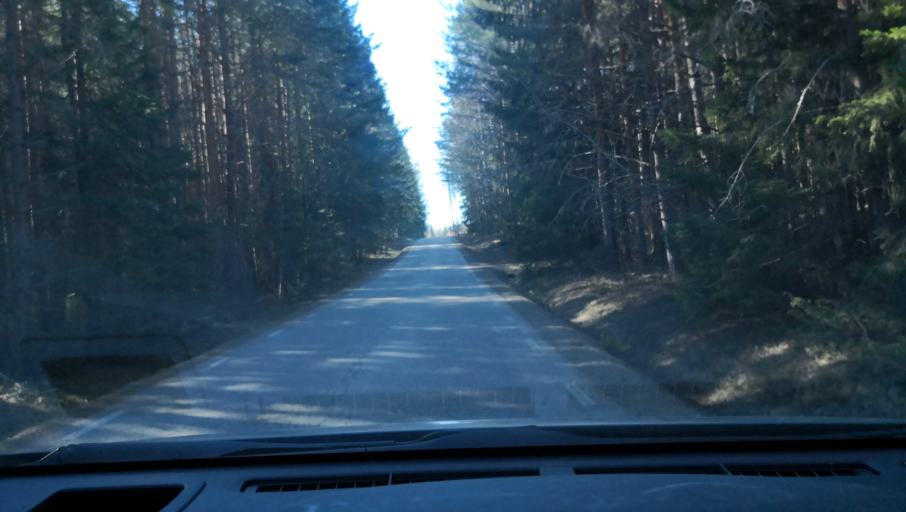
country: SE
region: Dalarna
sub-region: Avesta Kommun
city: Horndal
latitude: 60.0870
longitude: 16.4107
